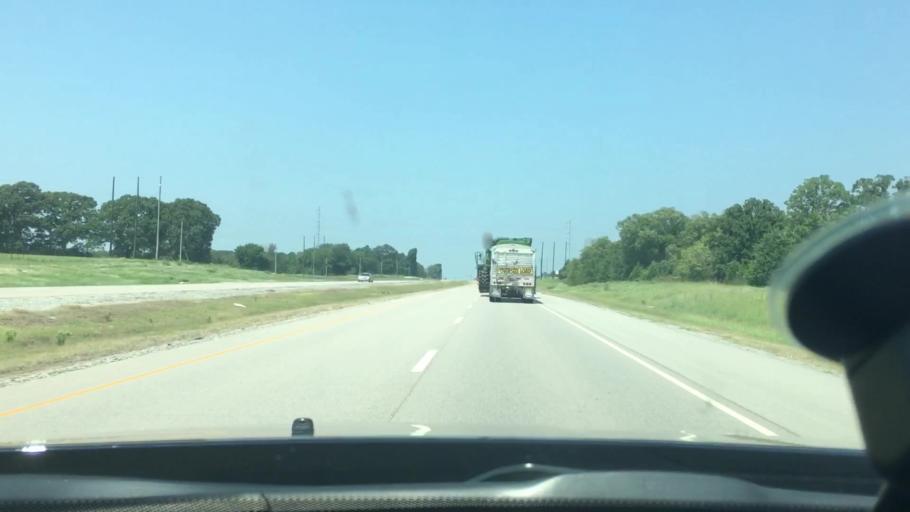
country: US
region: Oklahoma
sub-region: Atoka County
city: Atoka
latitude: 34.3278
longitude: -96.0460
